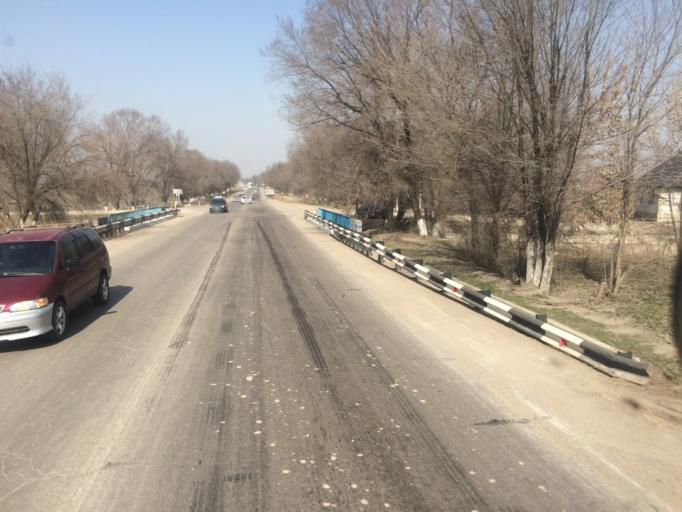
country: KZ
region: Almaty Oblysy
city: Burunday
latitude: 43.3264
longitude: 76.6625
